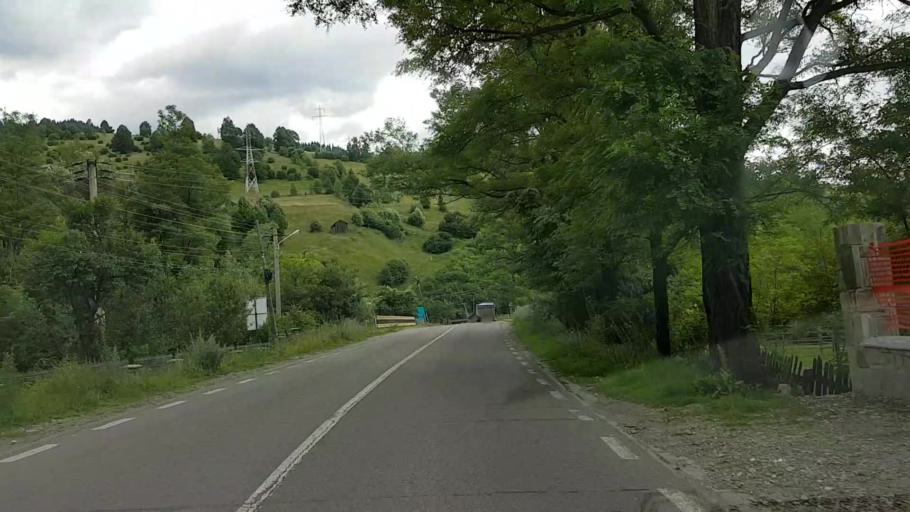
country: RO
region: Suceava
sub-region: Comuna Brosteni
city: Brosteni
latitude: 47.2363
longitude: 25.7403
